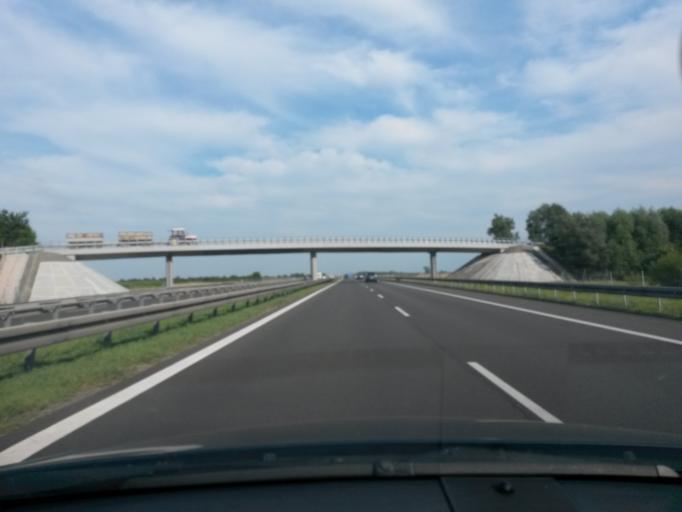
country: PL
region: Greater Poland Voivodeship
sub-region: Powiat slupecki
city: Ladek
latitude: 52.2127
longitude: 17.9856
